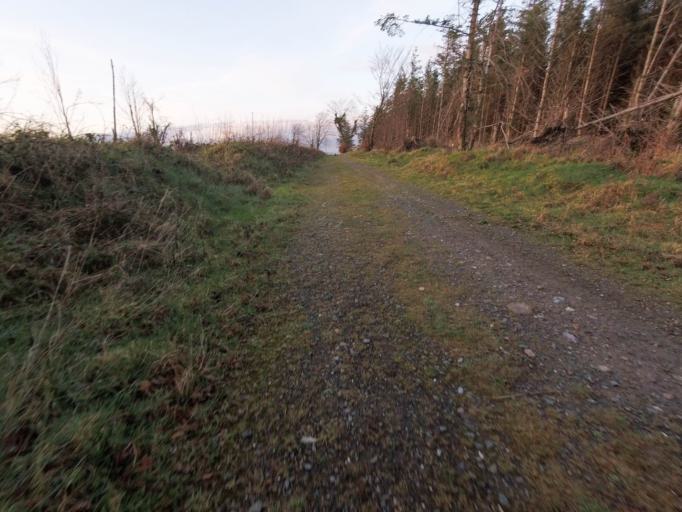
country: IE
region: Munster
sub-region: Waterford
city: Portlaw
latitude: 52.3083
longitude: -7.3478
